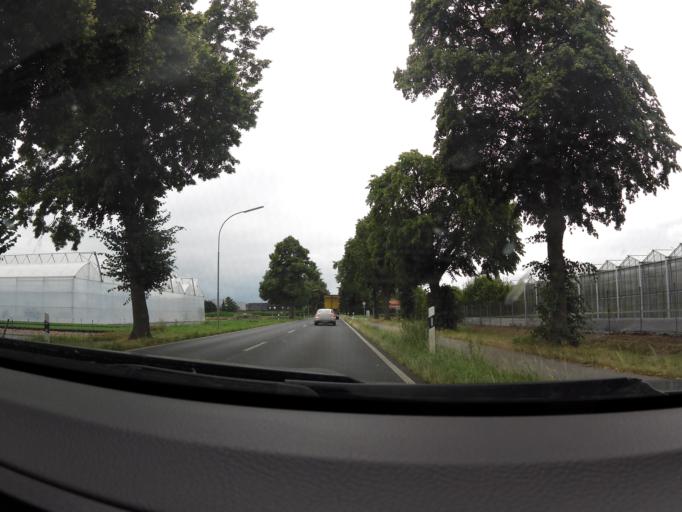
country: DE
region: North Rhine-Westphalia
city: Geldern
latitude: 51.4950
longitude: 6.3004
